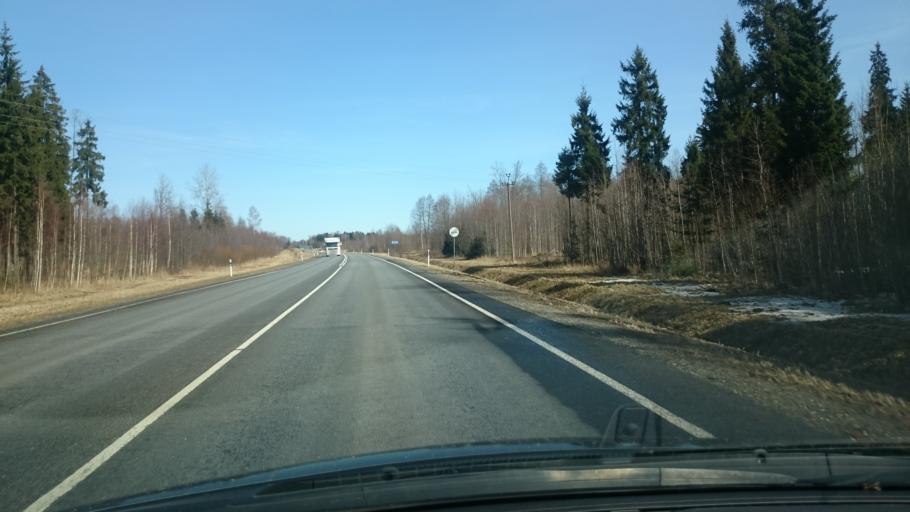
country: EE
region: Paernumaa
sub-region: Vaendra vald (alev)
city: Vandra
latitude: 58.6296
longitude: 24.9474
